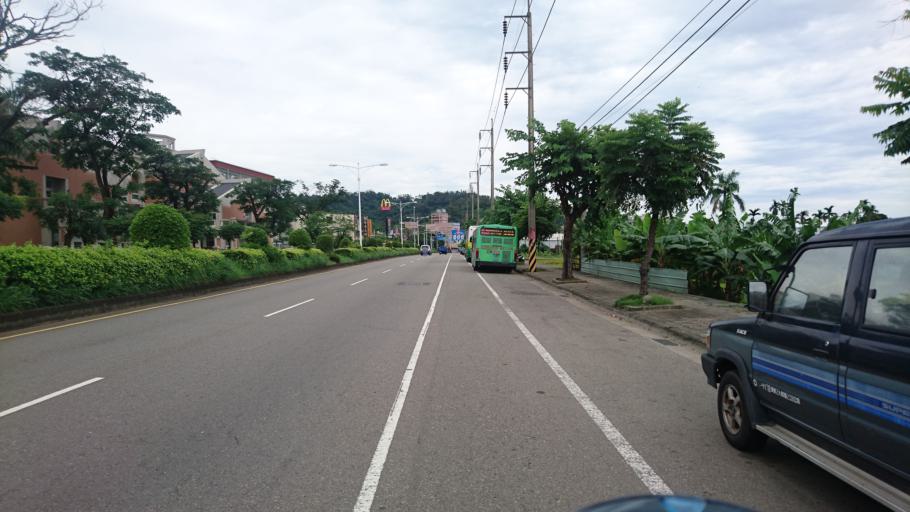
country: TW
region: Taiwan
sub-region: Taichung City
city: Taichung
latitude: 24.0573
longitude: 120.6956
